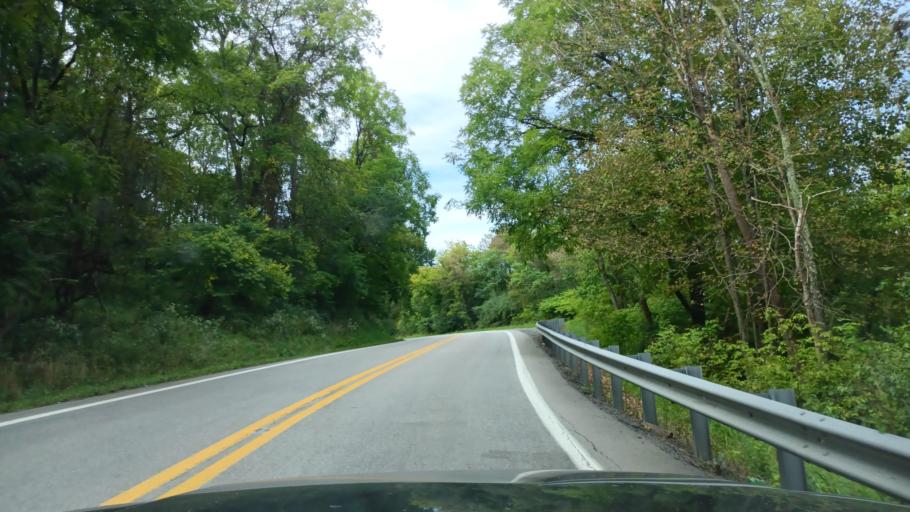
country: US
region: West Virginia
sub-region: Harrison County
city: Bridgeport
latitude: 39.3128
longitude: -80.1428
